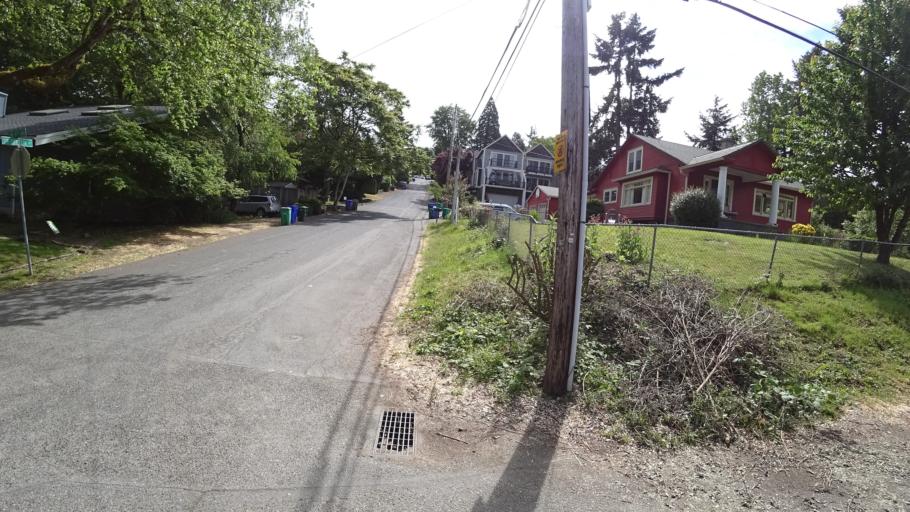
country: US
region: Oregon
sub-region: Clackamas County
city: Lake Oswego
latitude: 45.4611
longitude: -122.6870
